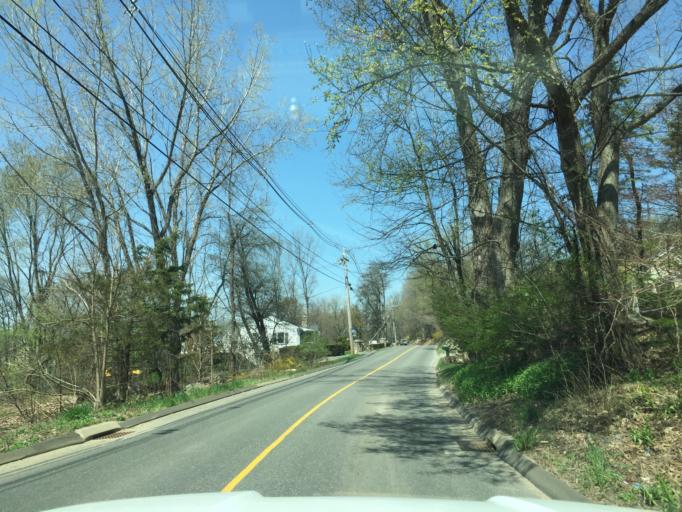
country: US
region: Connecticut
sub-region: Fairfield County
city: Bethel
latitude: 41.4055
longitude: -73.4020
